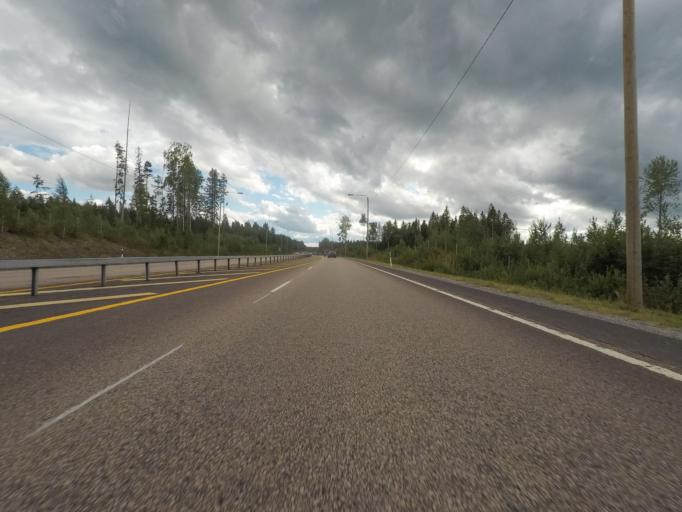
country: FI
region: Paijanne Tavastia
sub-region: Lahti
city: Heinola
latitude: 61.3584
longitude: 26.0422
